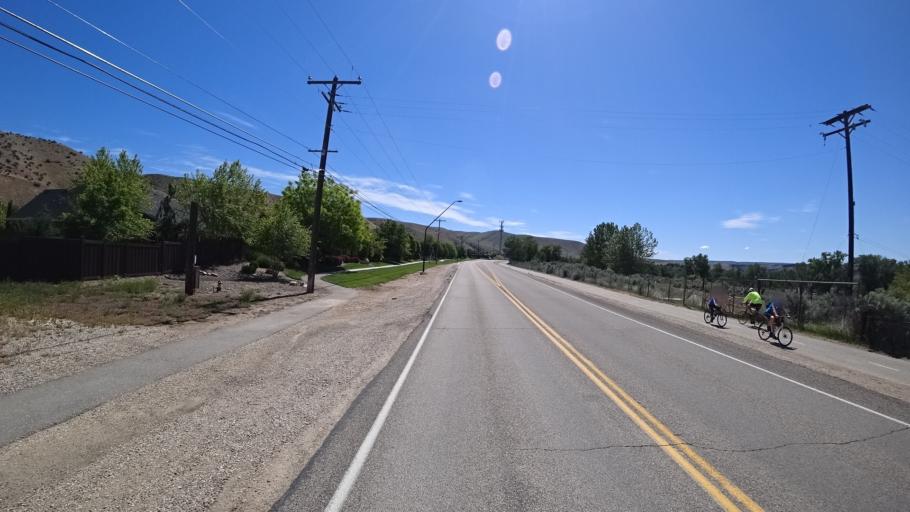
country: US
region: Idaho
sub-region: Ada County
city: Boise
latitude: 43.5630
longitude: -116.1079
